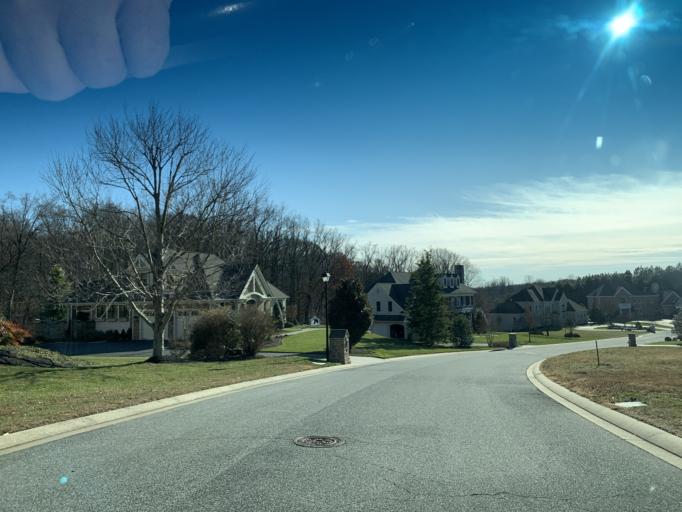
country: US
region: Maryland
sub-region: Harford County
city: Bel Air South
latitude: 39.5118
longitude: -76.3023
